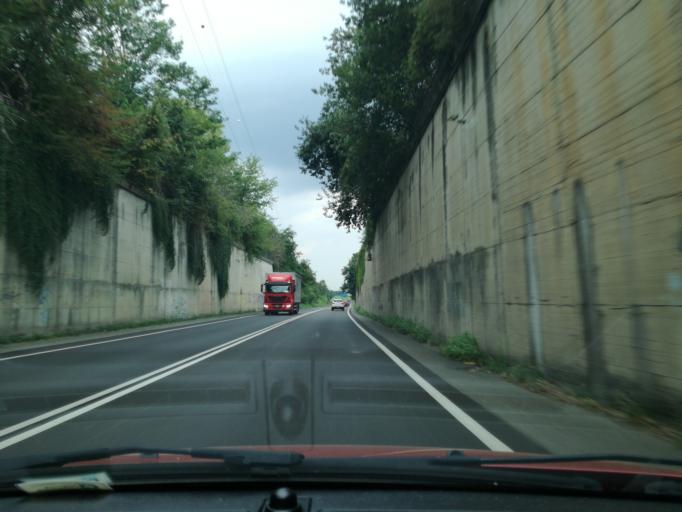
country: IT
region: Lombardy
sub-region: Provincia di Monza e Brianza
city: Velasca
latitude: 45.6393
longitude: 9.3503
